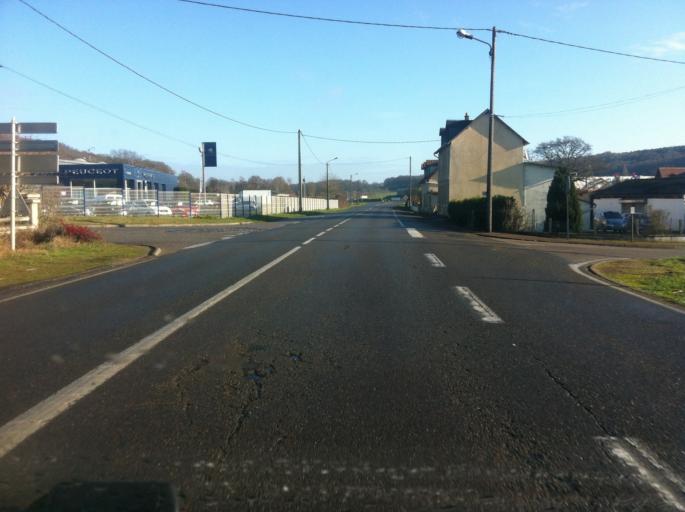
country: FR
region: Haute-Normandie
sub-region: Departement de la Seine-Maritime
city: Yainville
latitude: 49.4596
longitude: 0.8324
